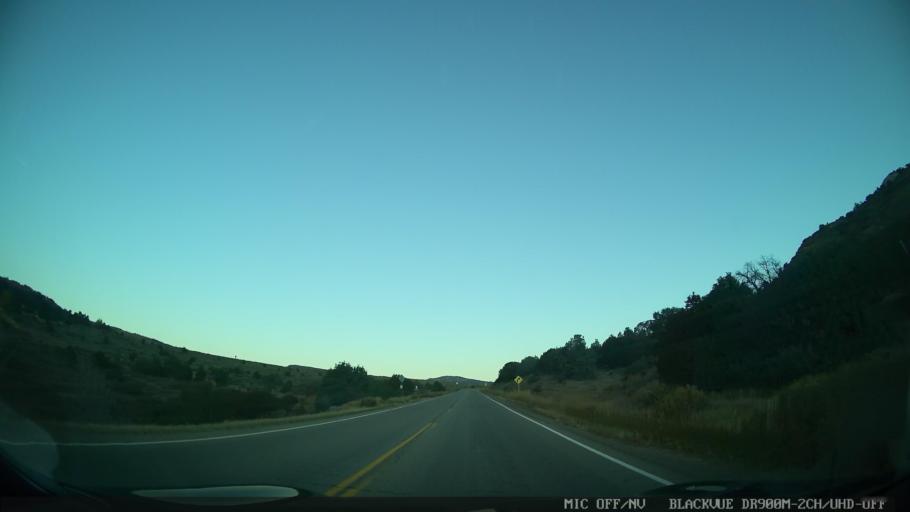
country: US
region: Colorado
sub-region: Eagle County
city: Edwards
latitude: 39.7047
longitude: -106.6814
